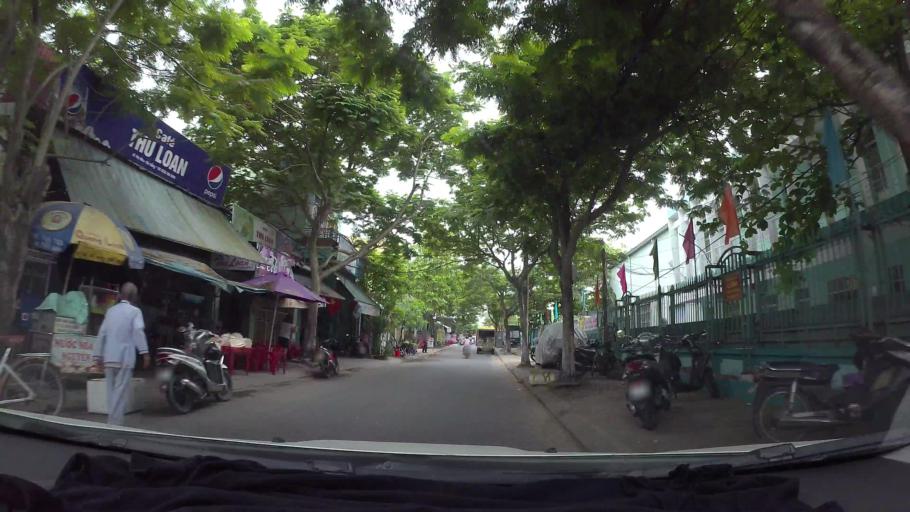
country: VN
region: Da Nang
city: Thanh Khe
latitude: 16.0666
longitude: 108.1795
